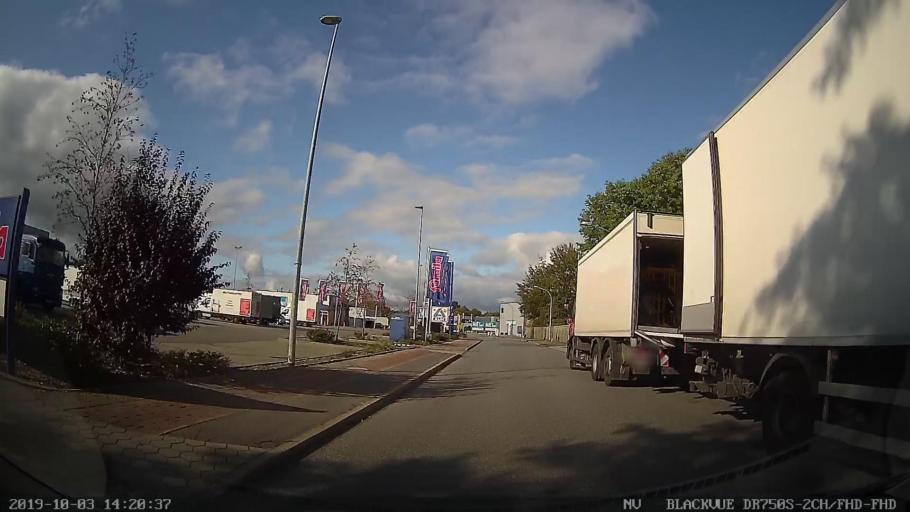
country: DE
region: Schleswig-Holstein
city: Pinneberg
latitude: 53.6719
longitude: 9.8024
